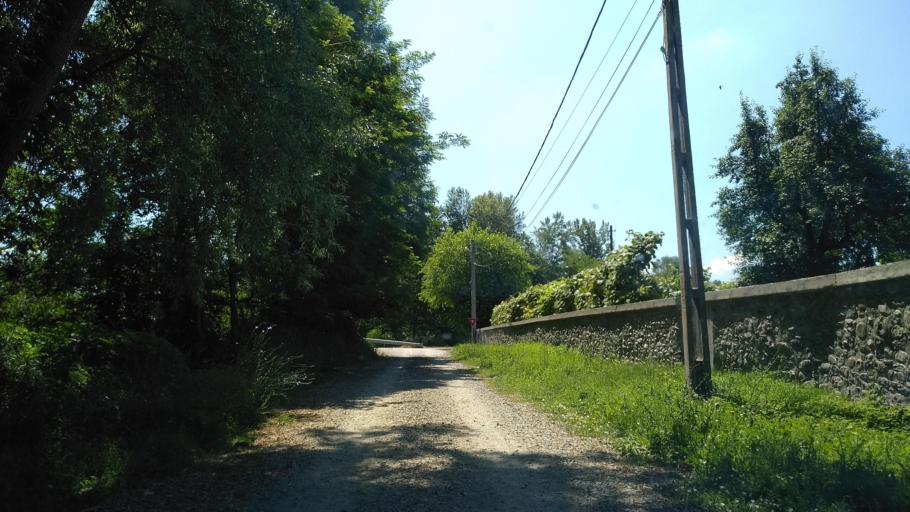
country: RO
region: Gorj
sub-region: Comuna Turcinesti
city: Turcinesti
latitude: 45.1177
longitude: 23.3152
